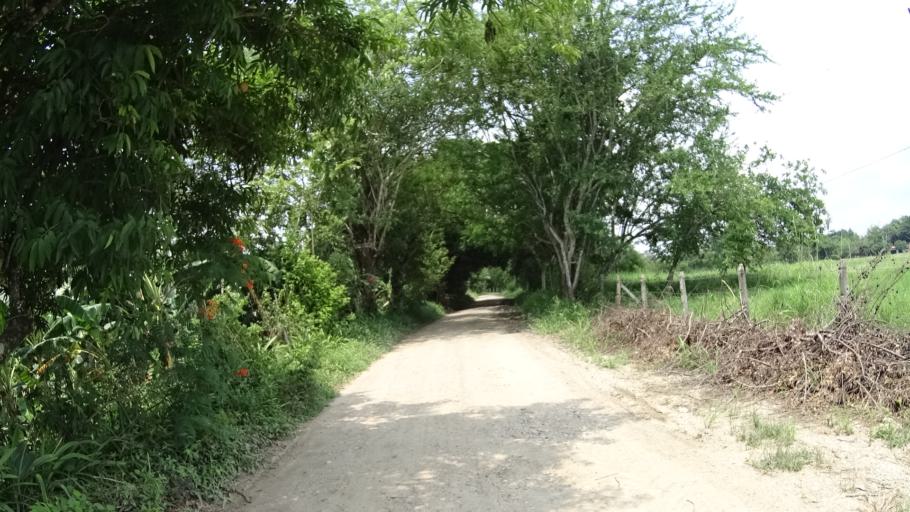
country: CO
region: Cundinamarca
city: Puerto Salgar
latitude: 5.5370
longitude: -74.6810
